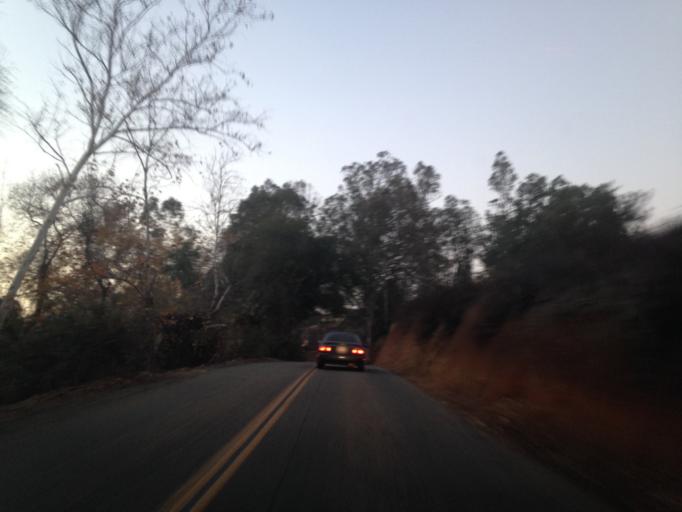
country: US
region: California
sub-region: San Diego County
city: Bonsall
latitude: 33.2584
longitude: -117.2123
